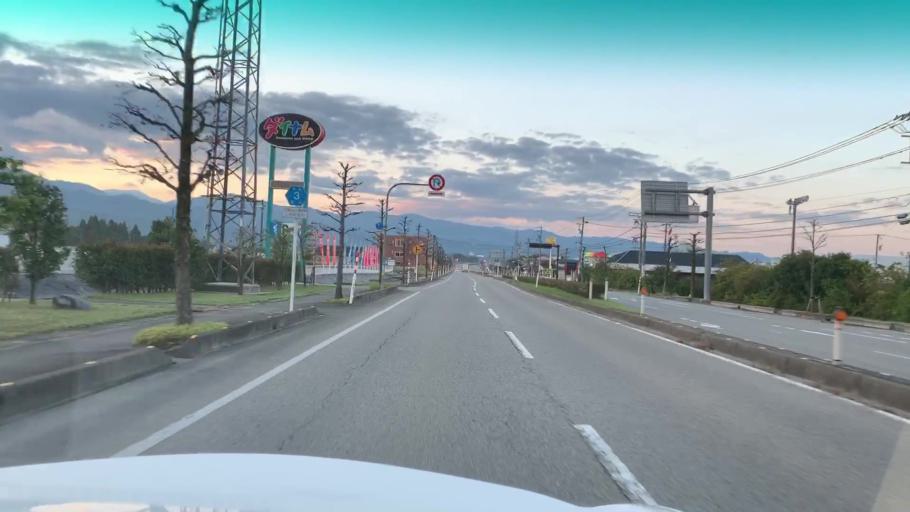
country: JP
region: Toyama
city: Kamiichi
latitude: 36.6999
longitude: 137.3425
